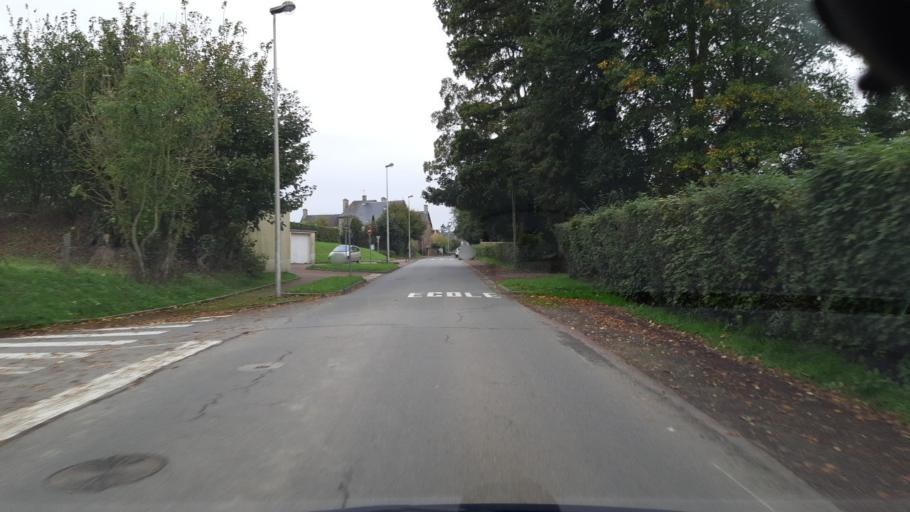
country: FR
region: Lower Normandy
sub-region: Departement de la Manche
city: Hambye
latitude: 48.9505
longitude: -1.2646
